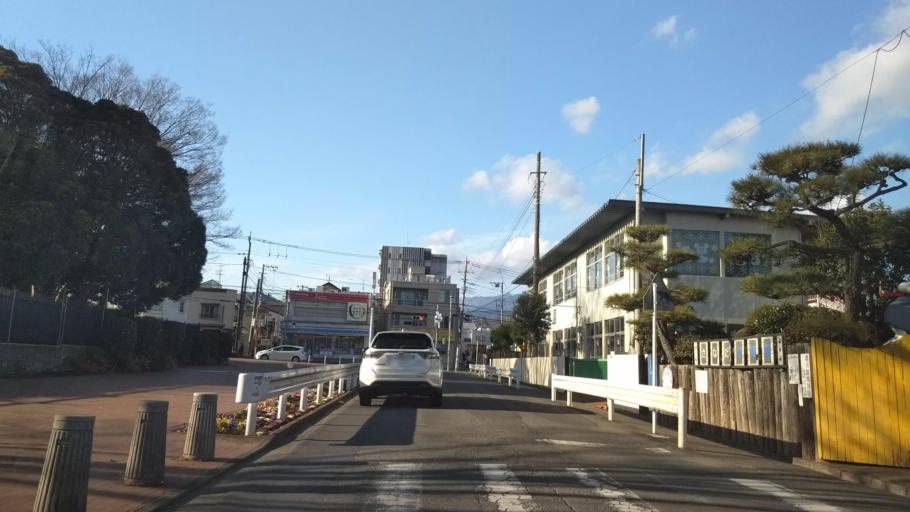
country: JP
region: Kanagawa
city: Isehara
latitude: 35.3668
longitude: 139.2739
